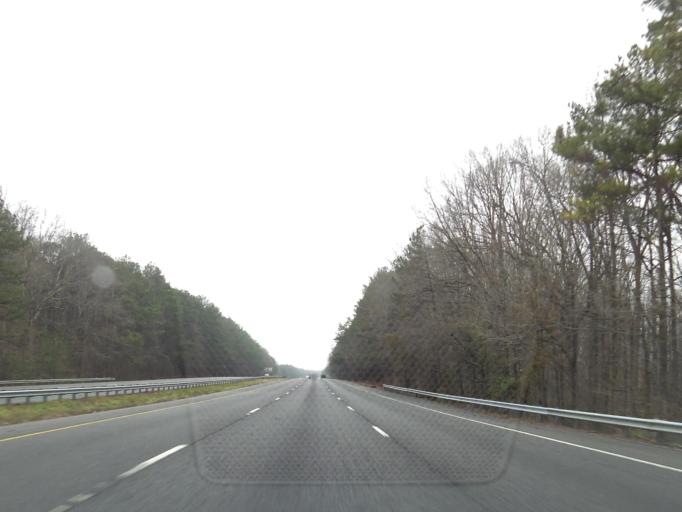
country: US
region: Georgia
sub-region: Butts County
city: Jackson
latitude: 33.1789
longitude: -84.0477
